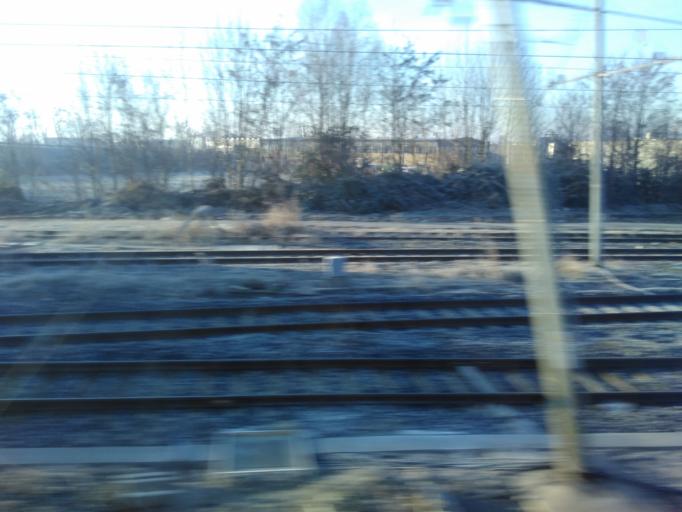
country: IT
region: Veneto
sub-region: Provincia di Vicenza
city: Grisignano di Zocco
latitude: 45.4849
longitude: 11.7138
